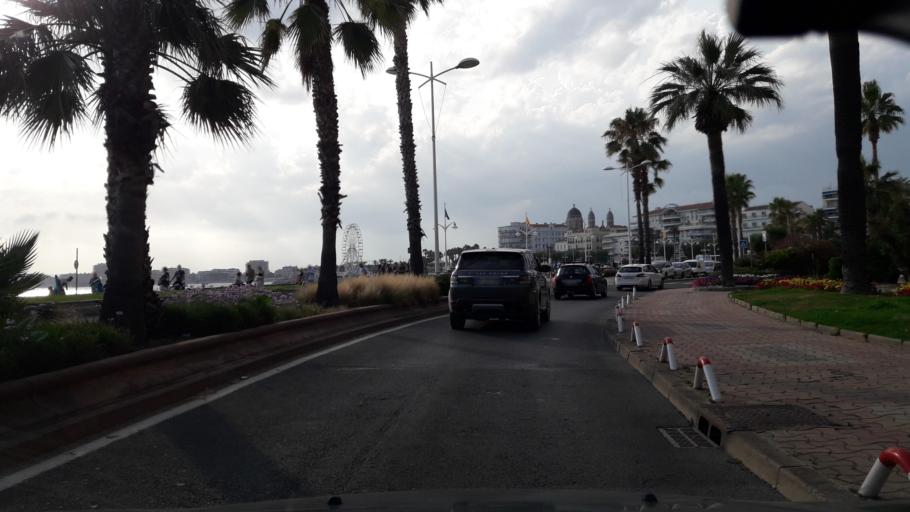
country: FR
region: Provence-Alpes-Cote d'Azur
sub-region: Departement du Var
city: Saint-Raphael
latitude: 43.4196
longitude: 6.7705
